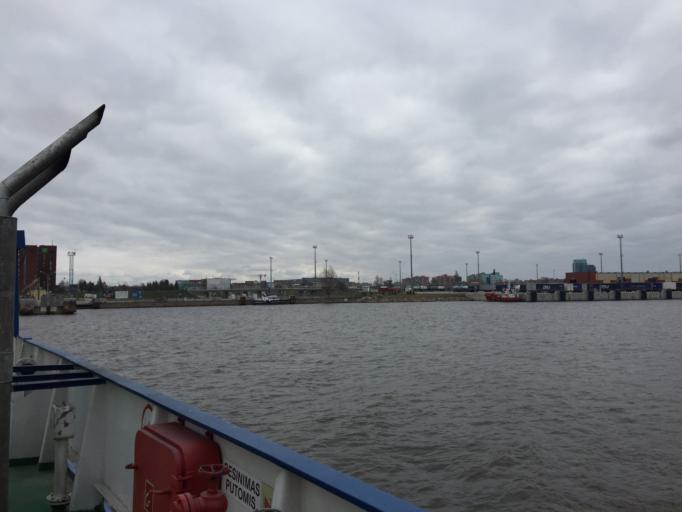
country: LT
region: Klaipedos apskritis
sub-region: Klaipeda
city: Klaipeda
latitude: 55.6877
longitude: 21.1354
